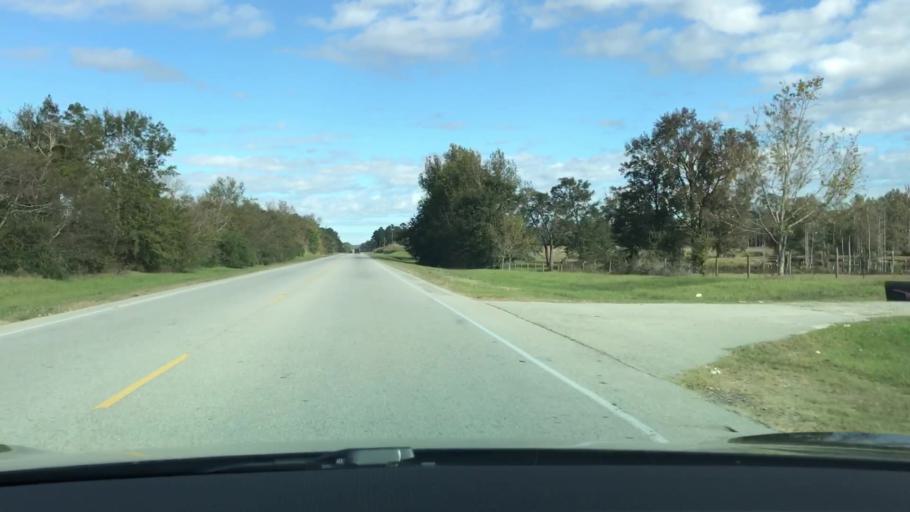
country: US
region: Georgia
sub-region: Jefferson County
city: Wadley
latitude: 32.9272
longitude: -82.3971
